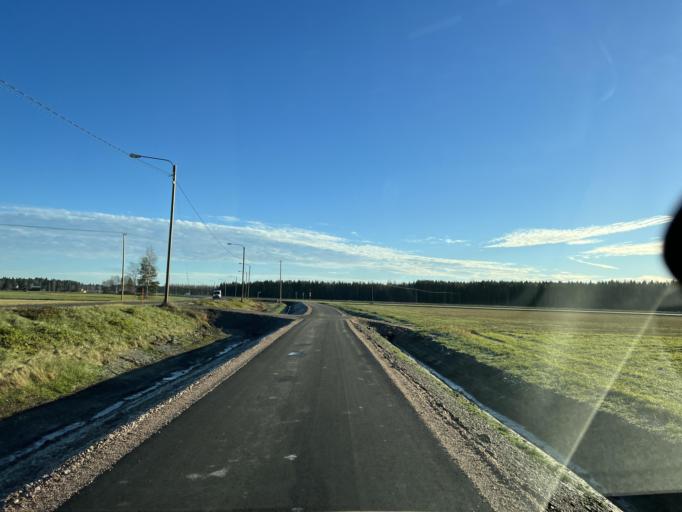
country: FI
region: Northern Ostrobothnia
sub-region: Nivala-Haapajaervi
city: Nivala
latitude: 63.9518
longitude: 24.8769
